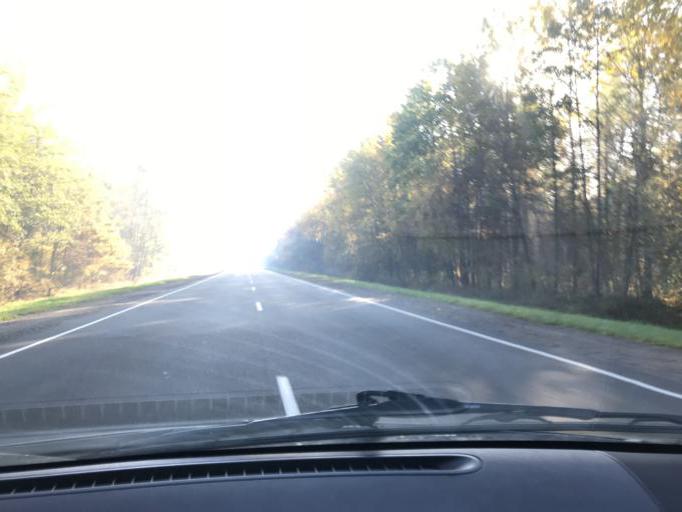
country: BY
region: Brest
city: Horad Luninyets
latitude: 52.3070
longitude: 26.6890
